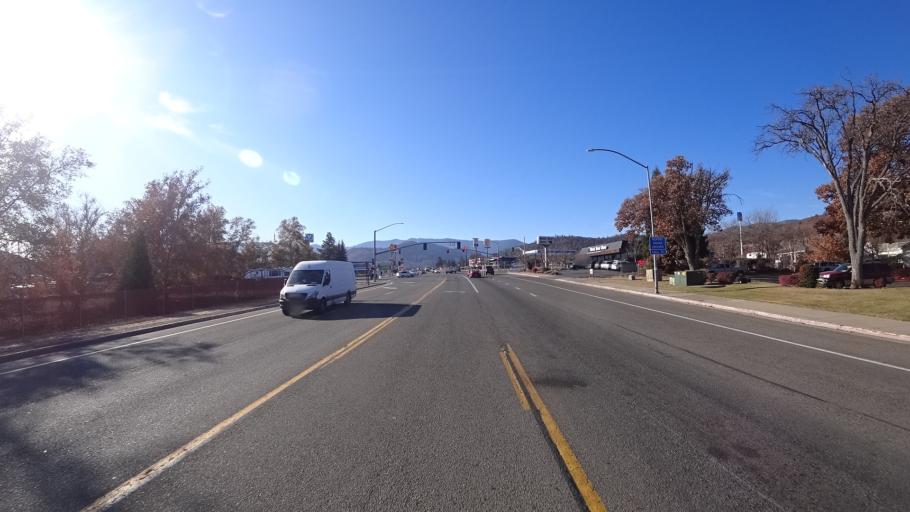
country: US
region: California
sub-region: Siskiyou County
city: Yreka
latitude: 41.7046
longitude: -122.6444
